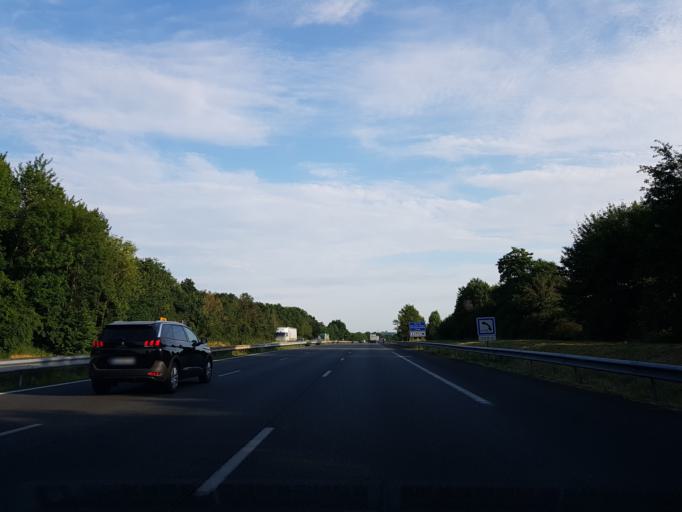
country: FR
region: Picardie
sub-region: Departement de l'Oise
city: Ressons-sur-Matz
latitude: 49.6107
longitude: 2.7552
